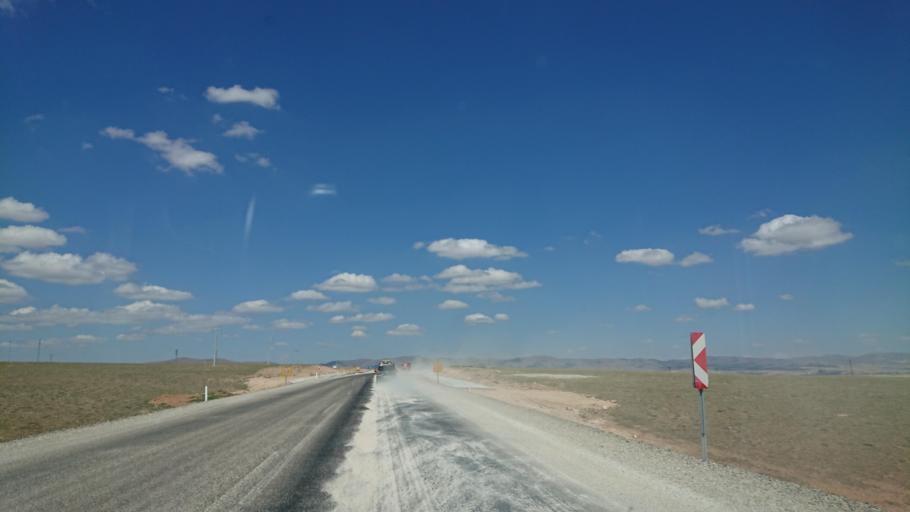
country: TR
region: Kirsehir
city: Kirsehir
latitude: 39.1300
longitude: 34.0386
